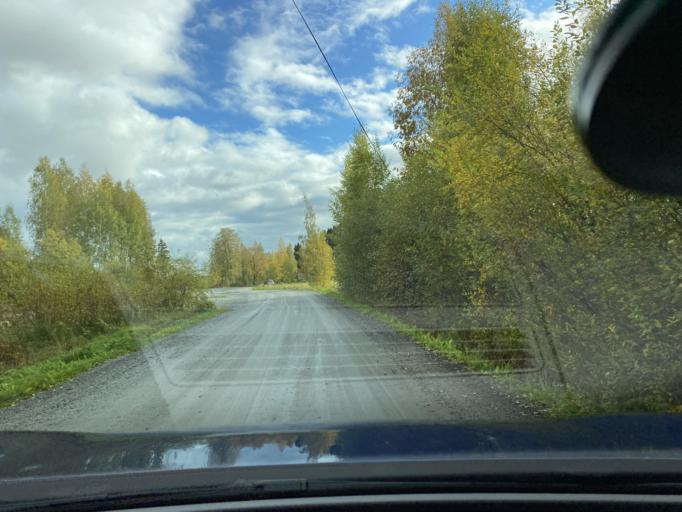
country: FI
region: Pirkanmaa
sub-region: Tampere
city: Nokia
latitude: 61.4721
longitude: 23.3537
